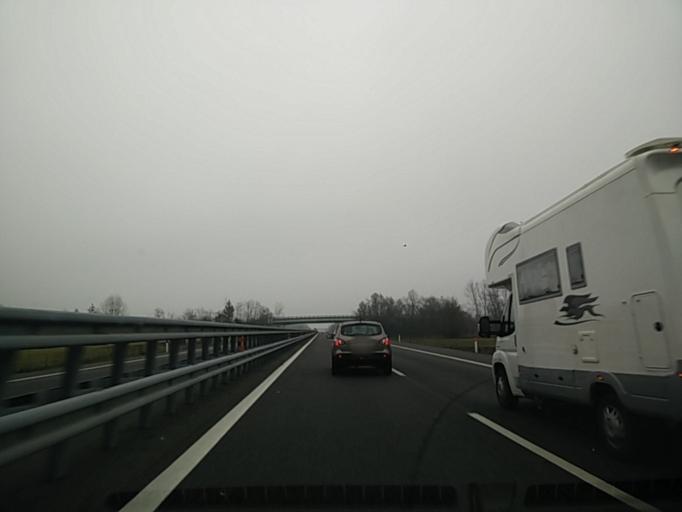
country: IT
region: Piedmont
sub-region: Provincia di Asti
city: Villafranca d'Asti
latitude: 44.9291
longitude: 8.0068
